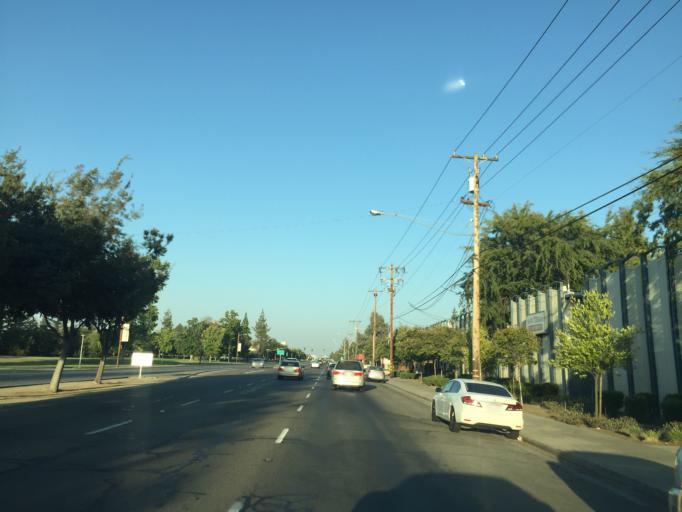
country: US
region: California
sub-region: Fresno County
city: Clovis
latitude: 36.8085
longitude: -119.7487
